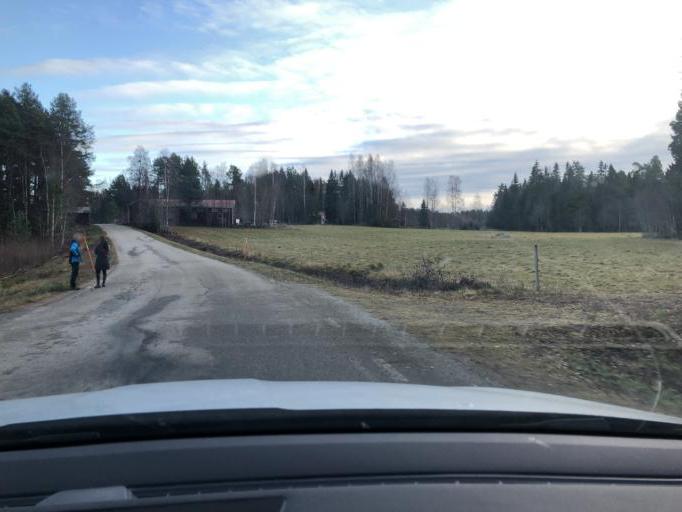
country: SE
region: Gaevleborg
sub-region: Hudiksvalls Kommun
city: Sorforsa
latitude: 61.7134
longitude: 16.9362
